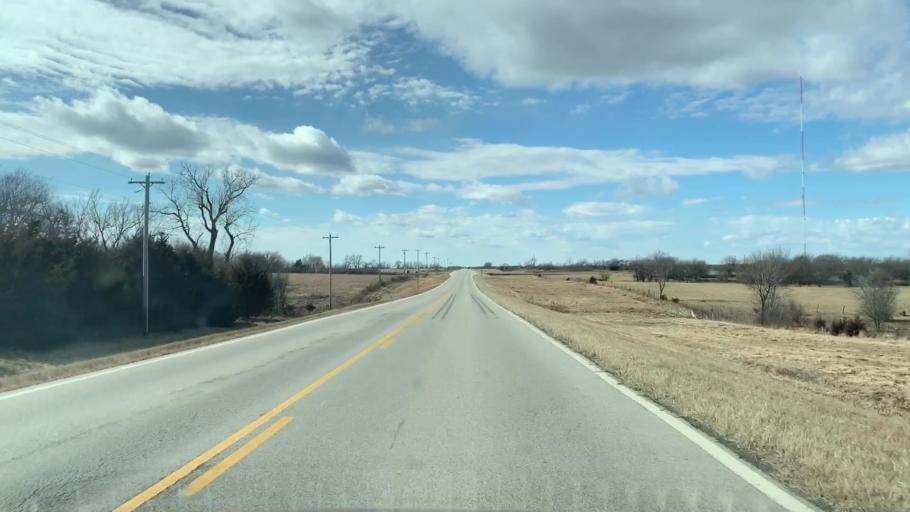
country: US
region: Kansas
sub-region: Neosho County
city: Erie
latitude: 37.5291
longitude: -95.3746
